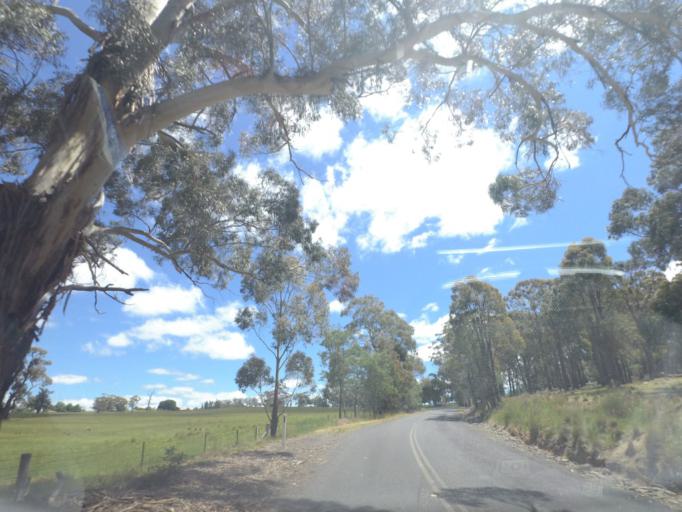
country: AU
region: Victoria
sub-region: Mount Alexander
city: Castlemaine
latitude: -37.3172
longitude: 144.1804
